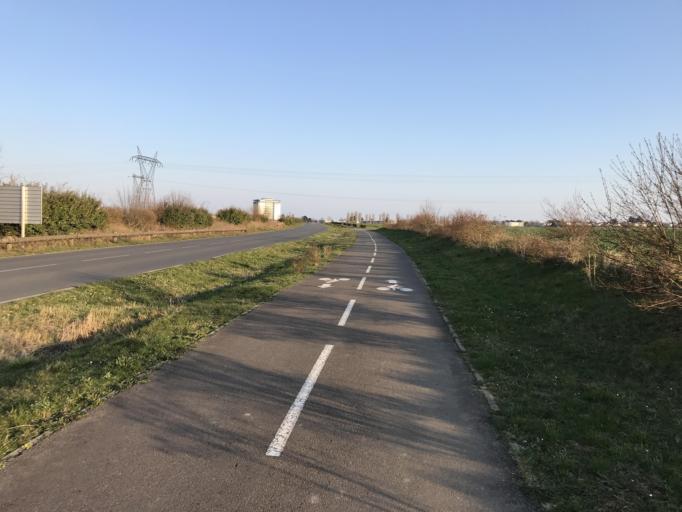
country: FR
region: Ile-de-France
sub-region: Departement de l'Essonne
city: Villejust
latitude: 48.6715
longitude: 2.2265
